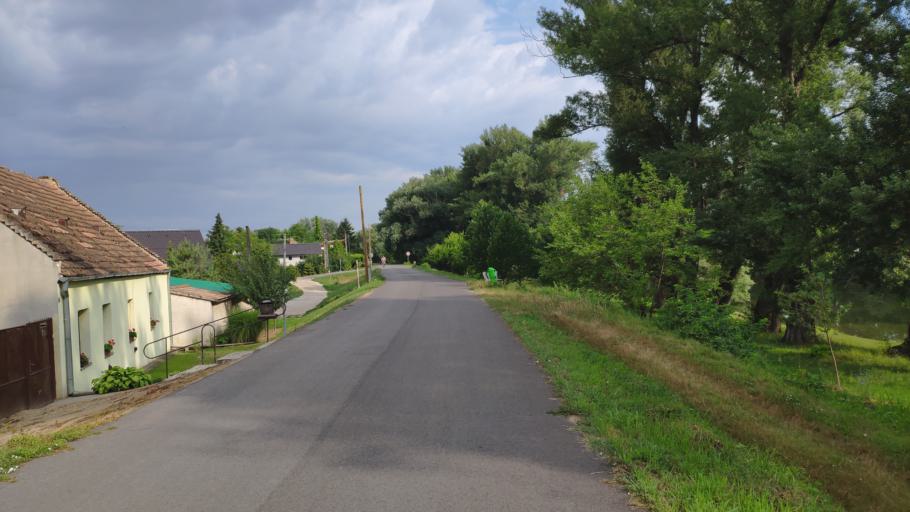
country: SK
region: Nitriansky
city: Kolarovo
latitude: 47.9181
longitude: 18.0035
